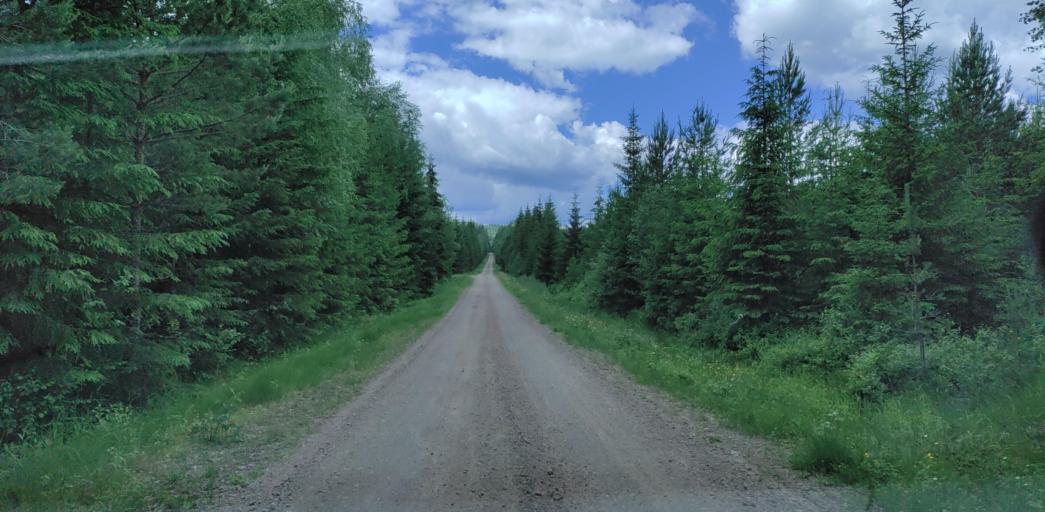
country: SE
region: Vaermland
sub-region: Hagfors Kommun
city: Ekshaerad
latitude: 60.0881
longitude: 13.4296
